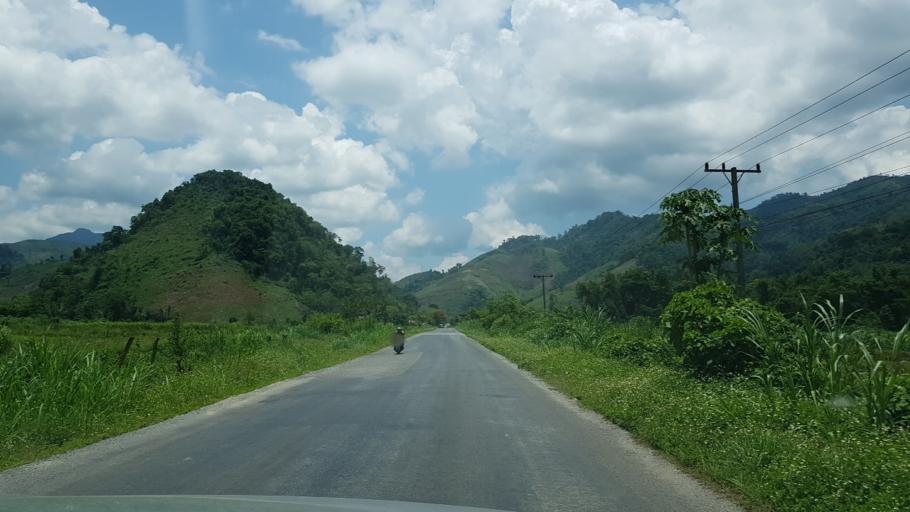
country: LA
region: Vientiane
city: Muang Kasi
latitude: 19.1302
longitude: 102.2721
